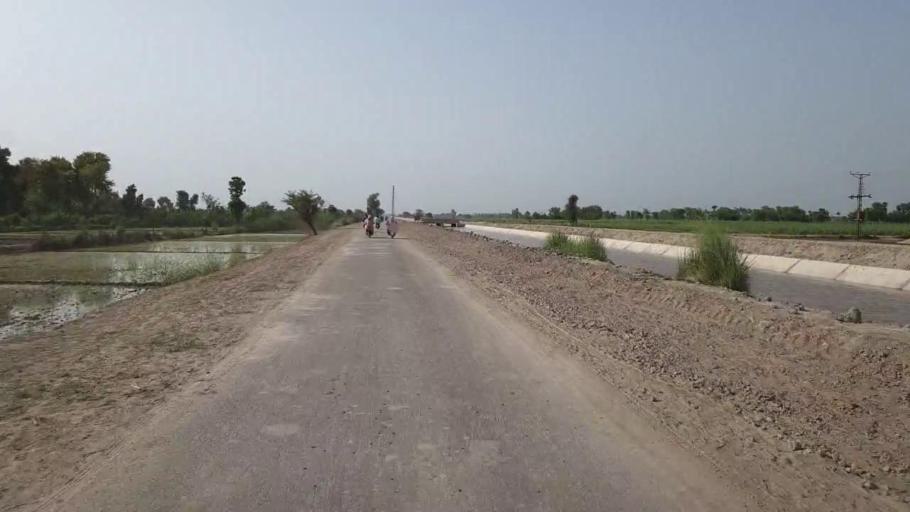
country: PK
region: Sindh
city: Daur
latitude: 26.3352
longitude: 68.1640
